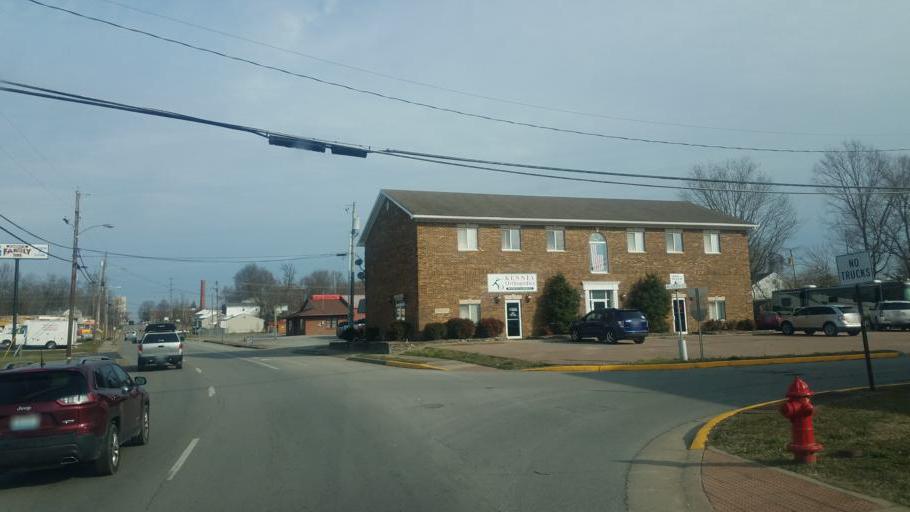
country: US
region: Kentucky
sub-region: Boyle County
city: Danville
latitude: 37.6371
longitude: -84.7733
